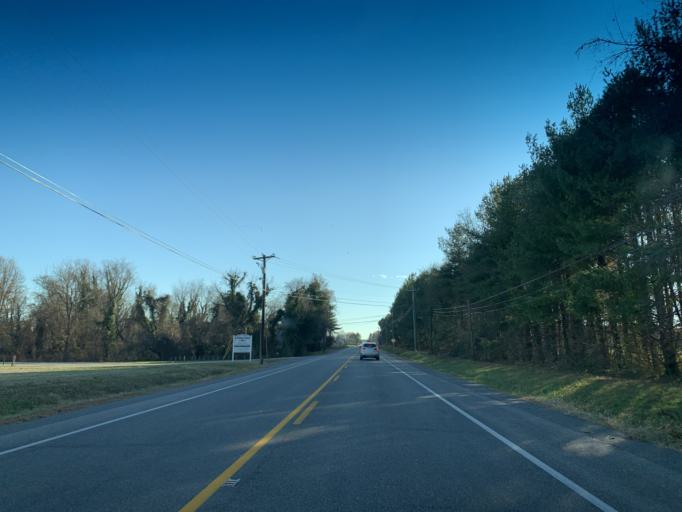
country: US
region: Delaware
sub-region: New Castle County
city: Middletown
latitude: 39.3539
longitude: -75.8772
